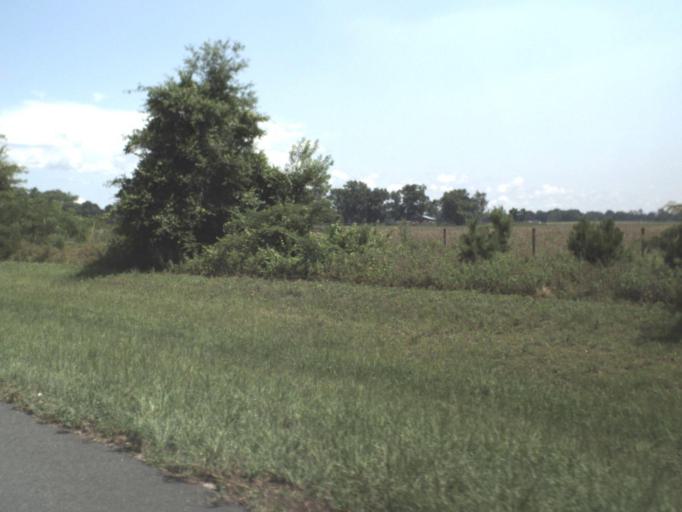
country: US
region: Florida
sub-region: Lafayette County
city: Mayo
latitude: 30.0770
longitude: -83.2111
